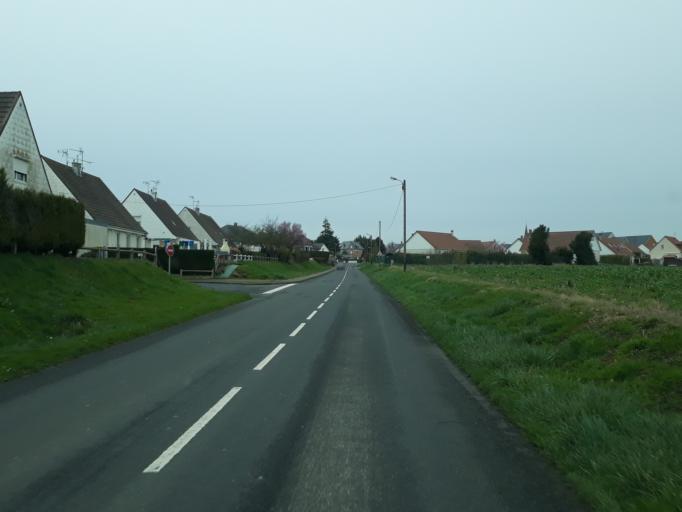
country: FR
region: Haute-Normandie
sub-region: Departement de la Seine-Maritime
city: Goderville
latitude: 49.6411
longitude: 0.3637
